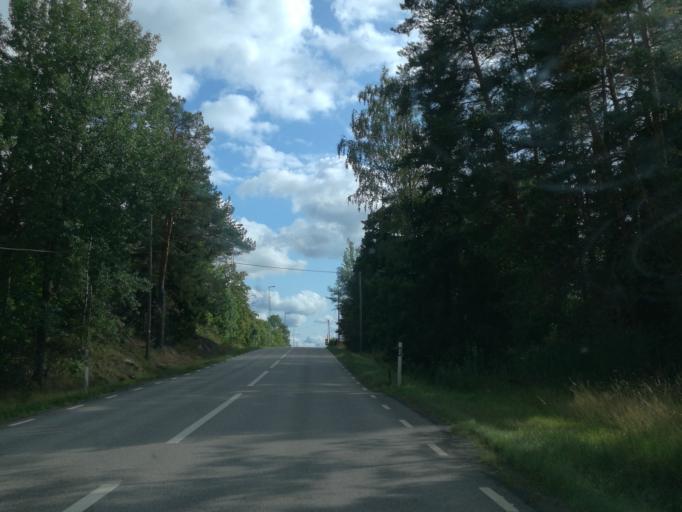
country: SE
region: Stockholm
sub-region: Vallentuna Kommun
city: Vallentuna
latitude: 59.5410
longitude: 17.9934
